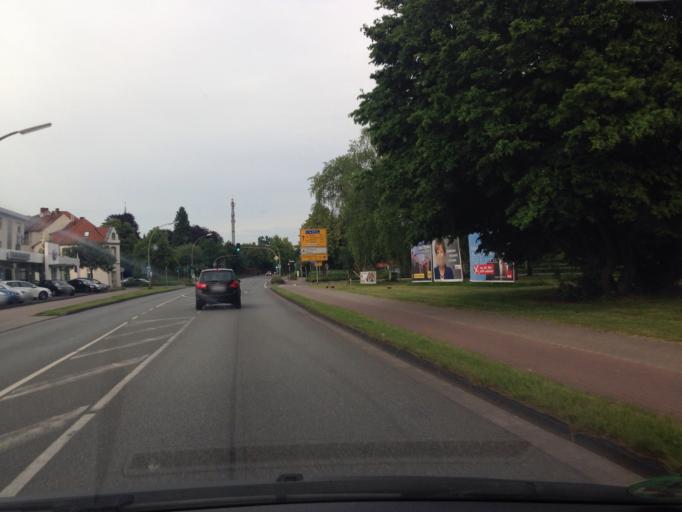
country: DE
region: North Rhine-Westphalia
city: Ludinghausen
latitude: 51.7679
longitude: 7.4354
